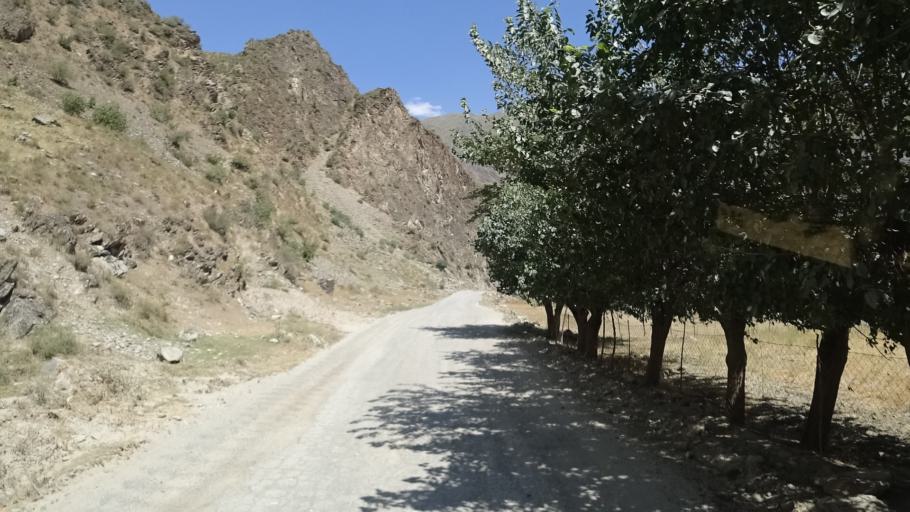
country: AF
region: Badakhshan
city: Maymay
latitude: 38.4441
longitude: 70.9381
